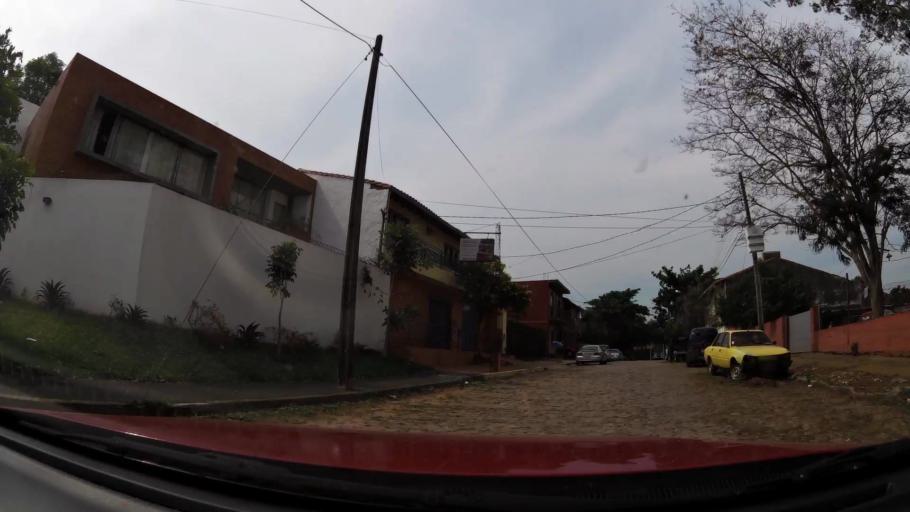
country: PY
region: Central
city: Fernando de la Mora
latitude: -25.2717
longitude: -57.5580
